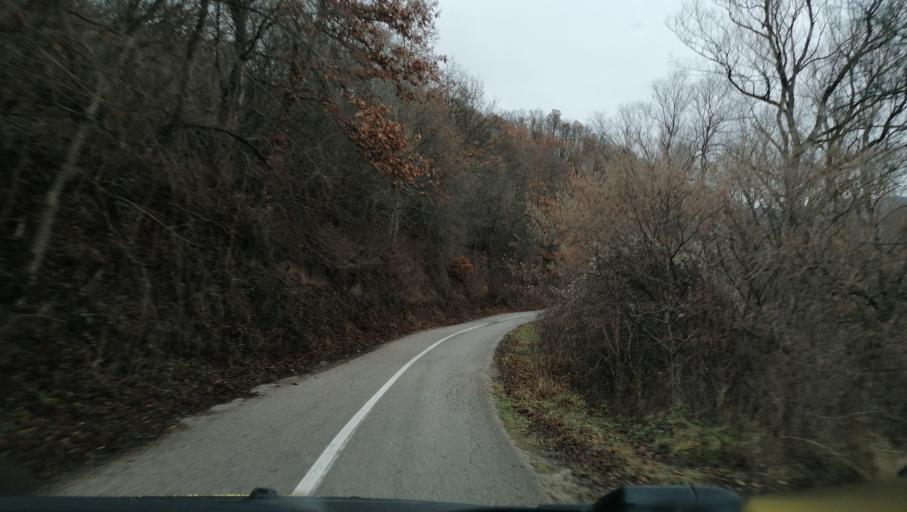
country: RS
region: Central Serbia
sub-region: Pirotski Okrug
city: Dimitrovgrad
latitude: 42.9637
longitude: 22.7826
